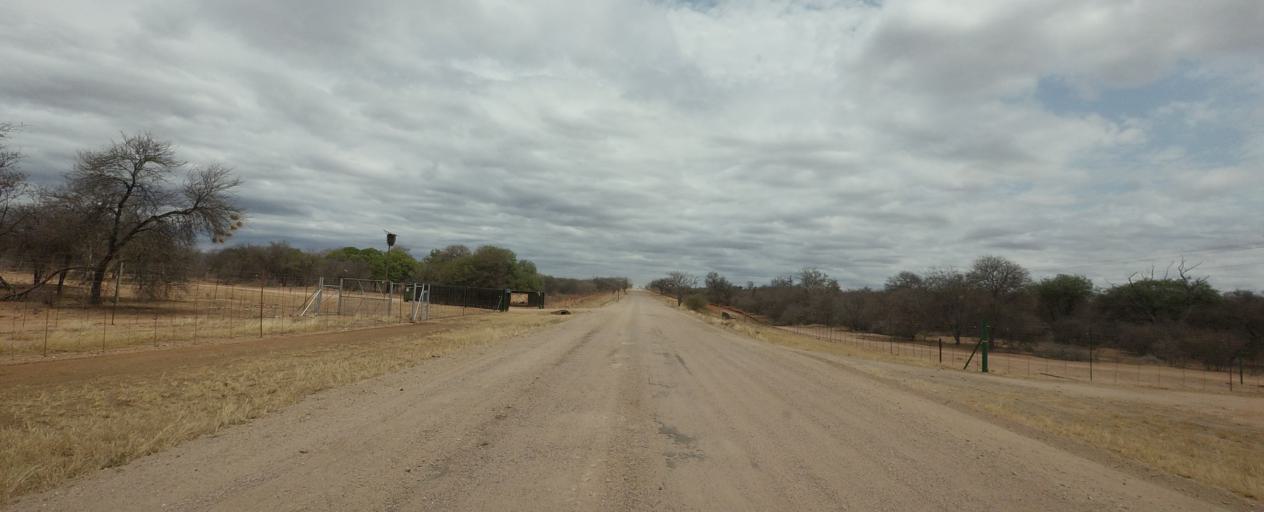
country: BW
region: Central
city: Mathathane
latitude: -22.6859
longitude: 28.6484
